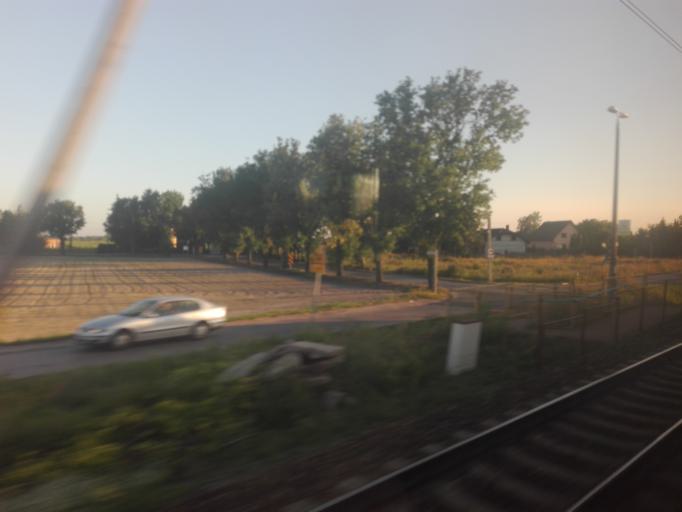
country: PL
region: Masovian Voivodeship
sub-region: Powiat warszawski zachodni
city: Ozarow Mazowiecki
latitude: 52.2079
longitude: 20.7556
